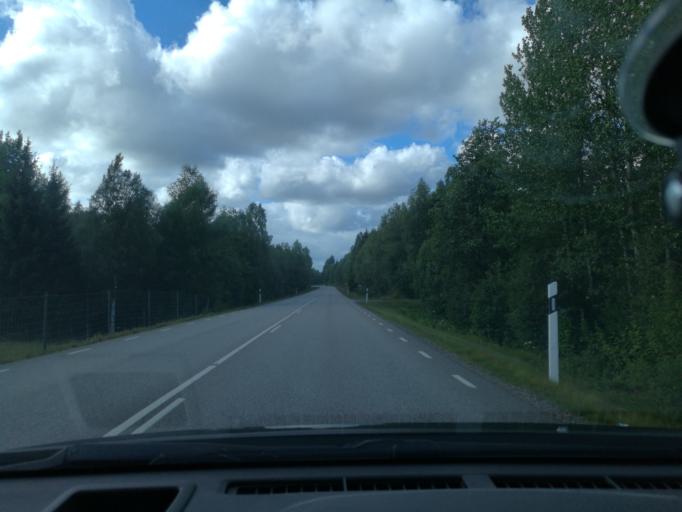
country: SE
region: Kronoberg
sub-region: Vaxjo Kommun
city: Braas
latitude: 57.0350
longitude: 15.0709
